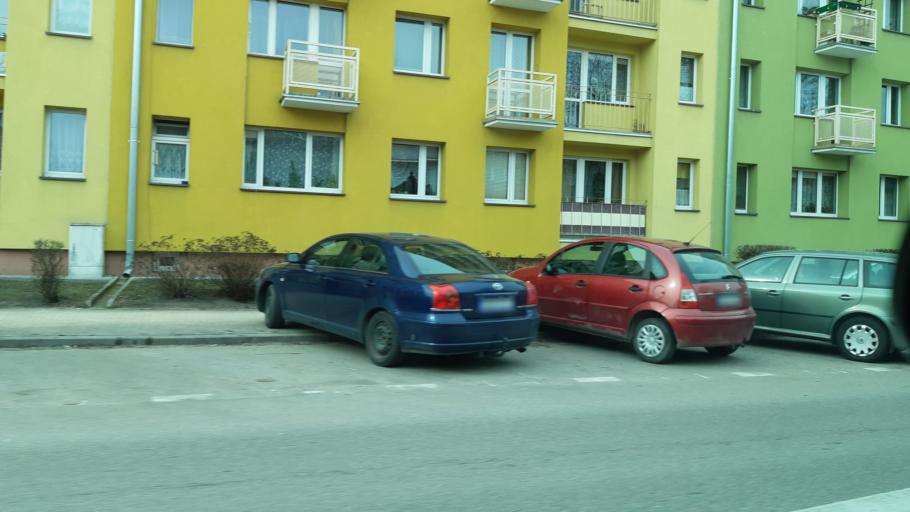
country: PL
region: Podlasie
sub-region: Suwalki
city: Suwalki
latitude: 54.0995
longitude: 22.9363
